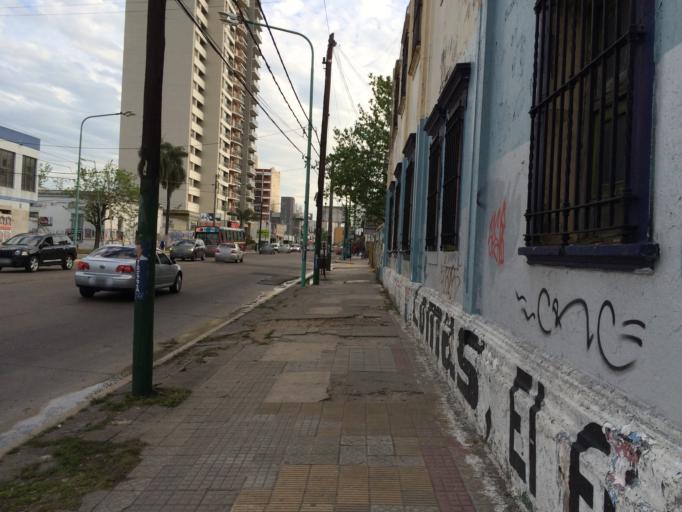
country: AR
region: Buenos Aires
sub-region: Partido de Lomas de Zamora
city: Lomas de Zamora
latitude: -34.7583
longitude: -58.3961
